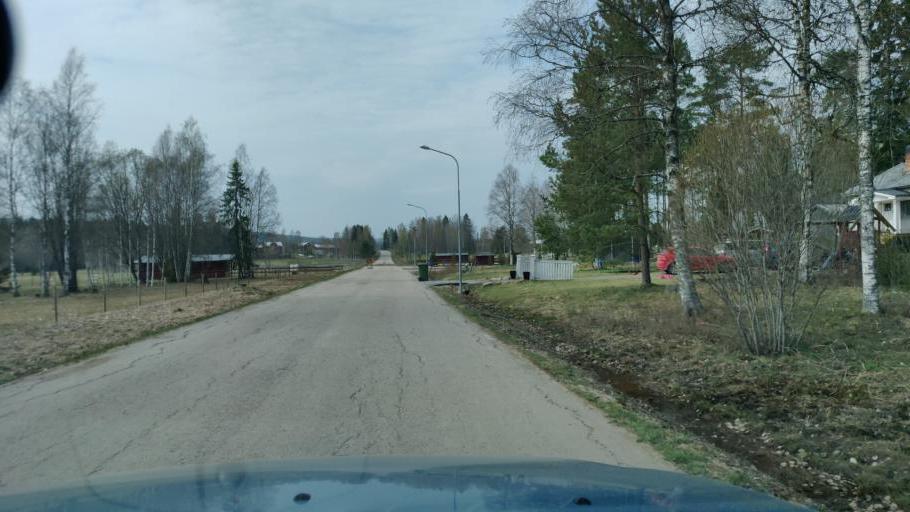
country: SE
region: Vaermland
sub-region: Munkfors Kommun
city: Munkfors
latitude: 59.8371
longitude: 13.5072
